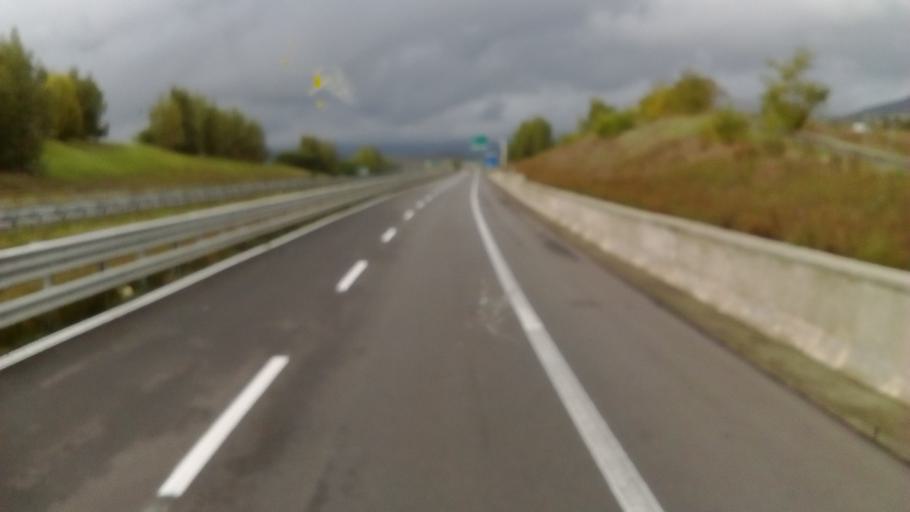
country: IT
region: Sicily
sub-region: Enna
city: Assoro
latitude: 37.5676
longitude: 14.4106
